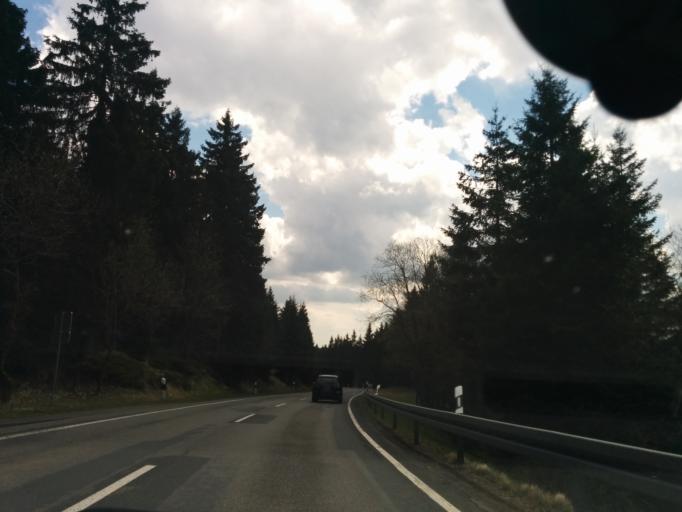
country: DE
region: Lower Saxony
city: Sankt Andreasberg
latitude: 51.7384
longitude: 10.5231
